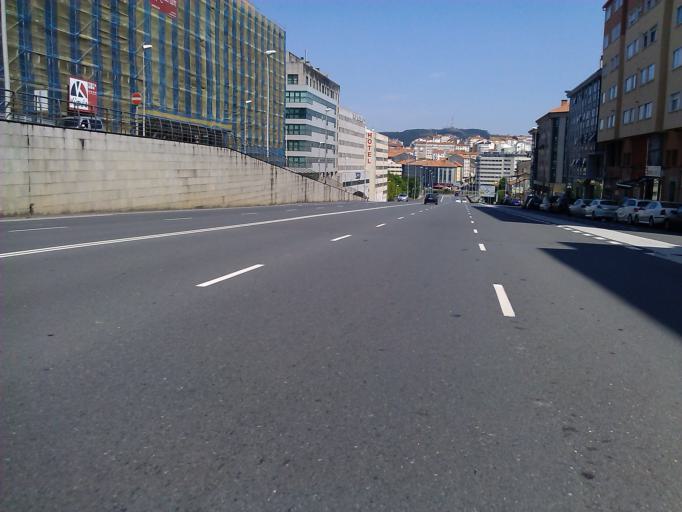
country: ES
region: Galicia
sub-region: Provincia da Coruna
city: Santiago de Compostela
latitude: 42.8635
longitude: -8.5424
